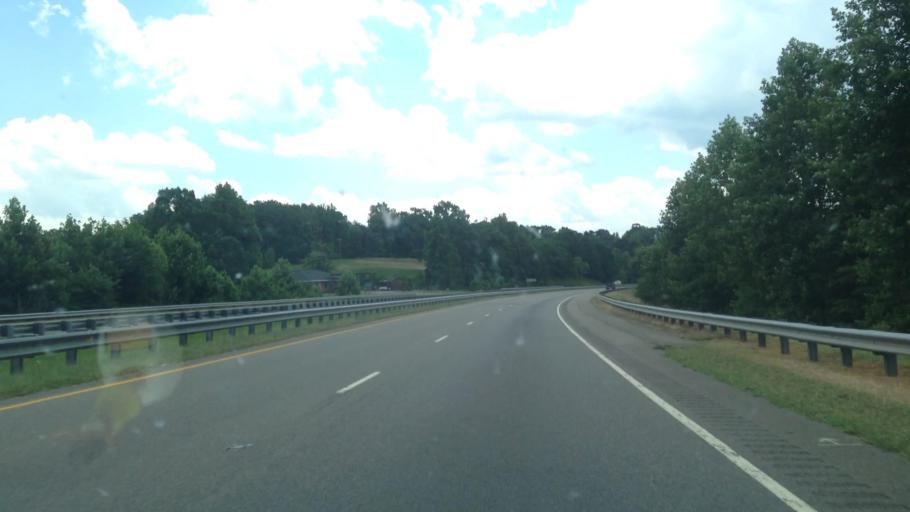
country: US
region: North Carolina
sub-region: Rockingham County
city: Stoneville
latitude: 36.5177
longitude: -79.9174
